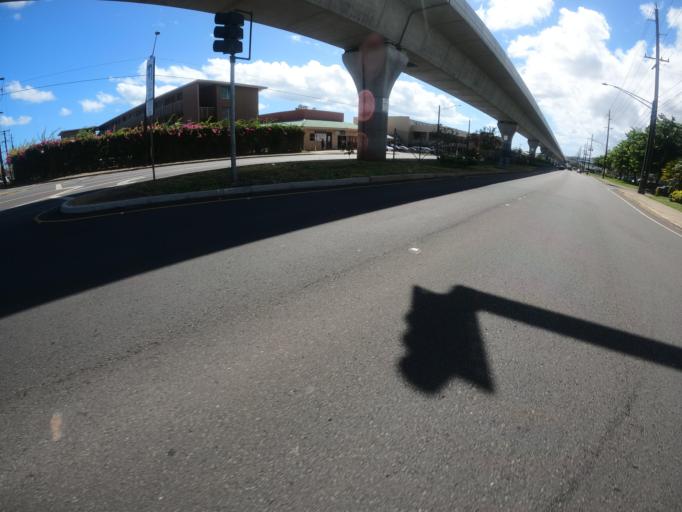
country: US
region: Hawaii
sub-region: Honolulu County
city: Waipahu
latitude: 21.3809
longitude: -158.0161
